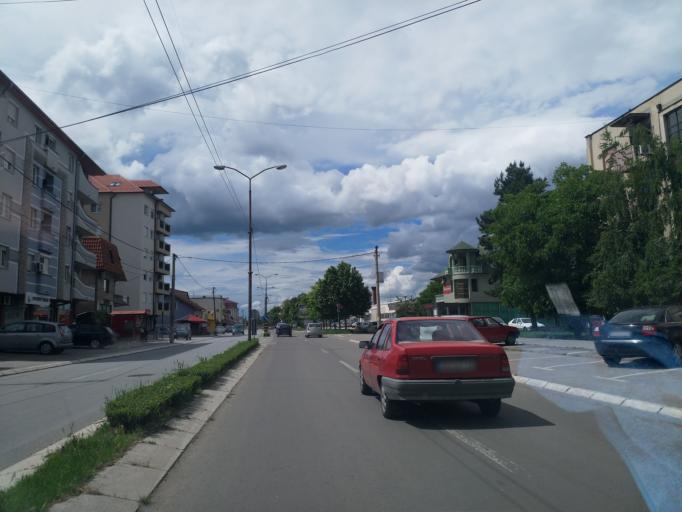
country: RS
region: Central Serbia
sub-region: Pomoravski Okrug
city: Paracin
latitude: 43.8653
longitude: 21.4078
